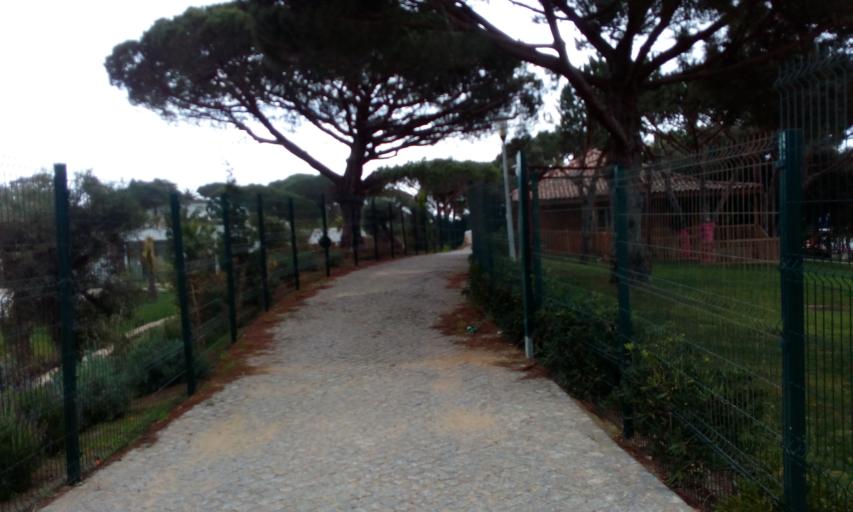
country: PT
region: Faro
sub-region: Albufeira
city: Albufeira
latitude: 37.0914
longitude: -8.2079
